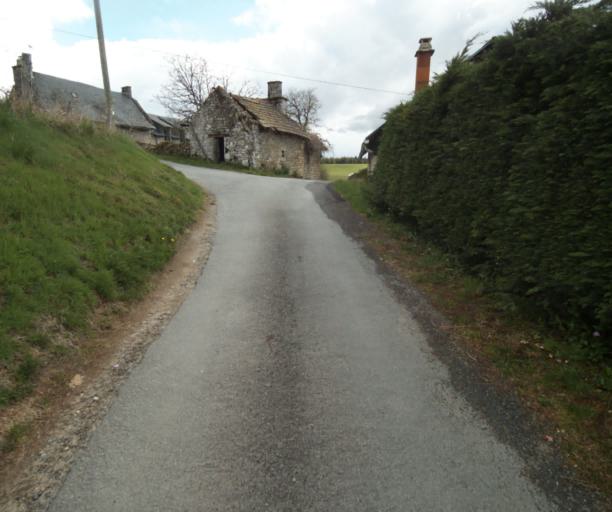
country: FR
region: Limousin
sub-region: Departement de la Correze
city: Correze
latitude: 45.3049
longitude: 1.8886
